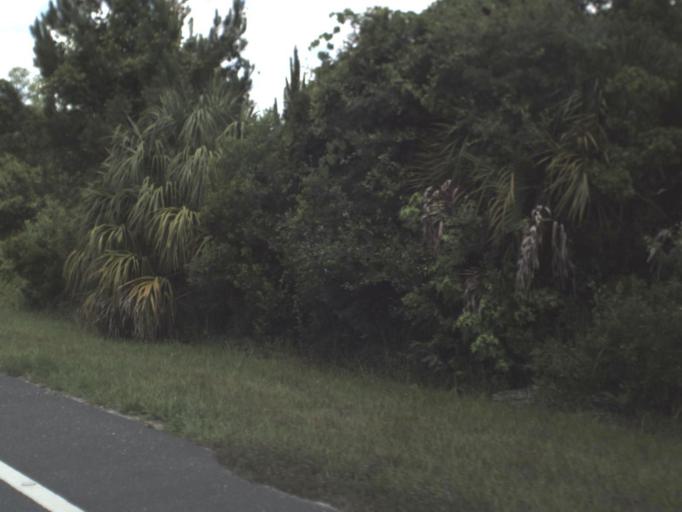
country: US
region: Florida
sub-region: Levy County
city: Chiefland
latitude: 29.2115
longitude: -82.9765
